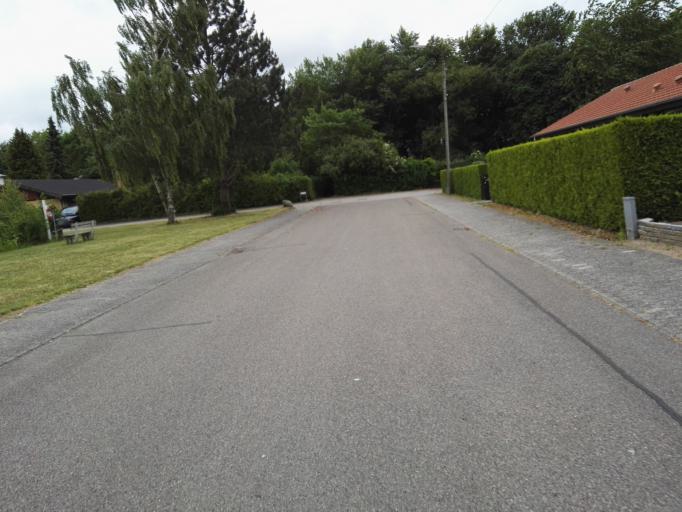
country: DK
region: Capital Region
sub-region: Ballerup Kommune
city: Ballerup
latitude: 55.7371
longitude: 12.3723
